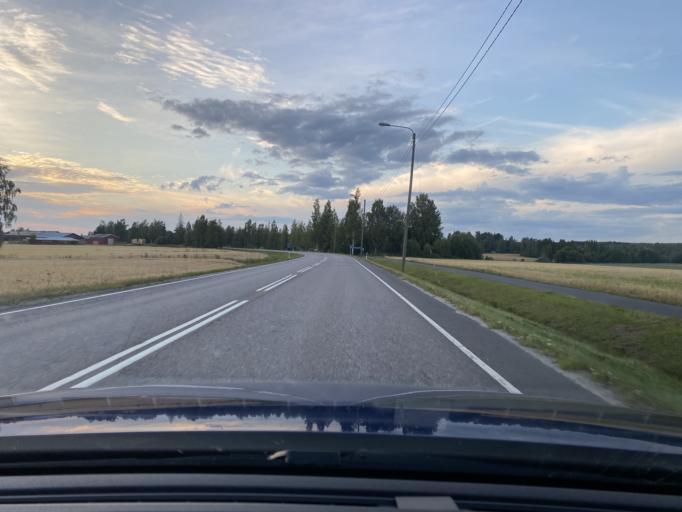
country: FI
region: Satakunta
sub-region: Pohjois-Satakunta
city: Kankaanpaeae
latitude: 61.7579
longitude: 22.5043
